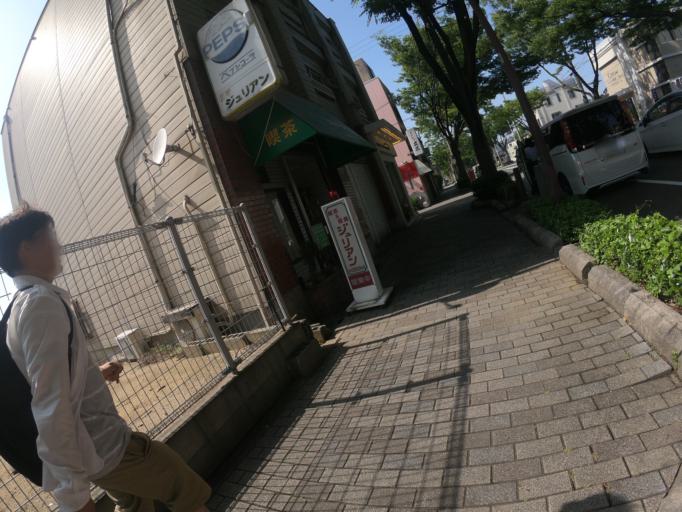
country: JP
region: Osaka
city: Sakai
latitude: 34.5724
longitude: 135.4900
